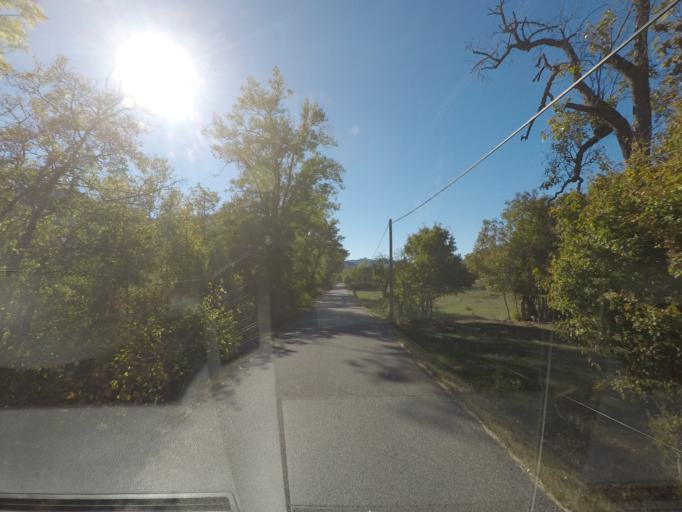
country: FR
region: Provence-Alpes-Cote d'Azur
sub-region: Departement des Hautes-Alpes
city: Serres
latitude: 44.4676
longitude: 5.4989
